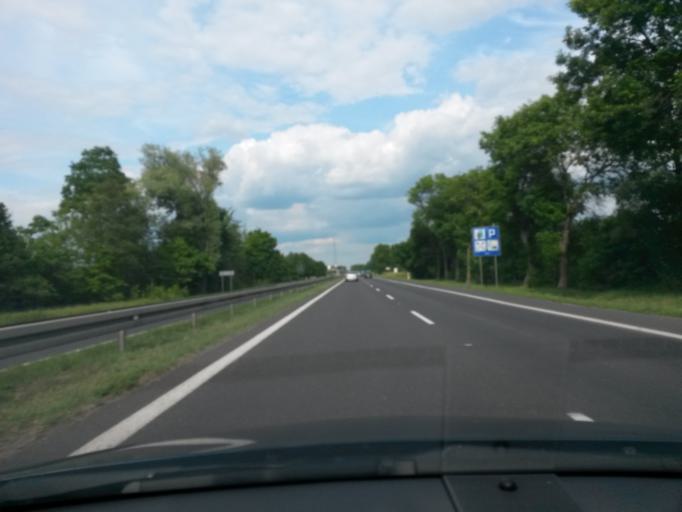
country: PL
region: Lodz Voivodeship
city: Zabia Wola
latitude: 52.0250
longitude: 20.6577
